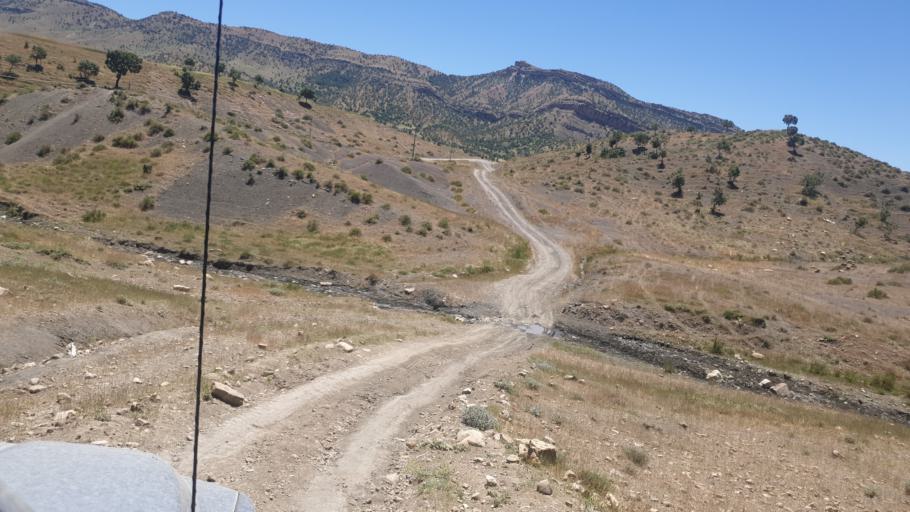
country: IQ
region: Arbil
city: Nahiyat Hiran
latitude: 36.2018
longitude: 44.4231
